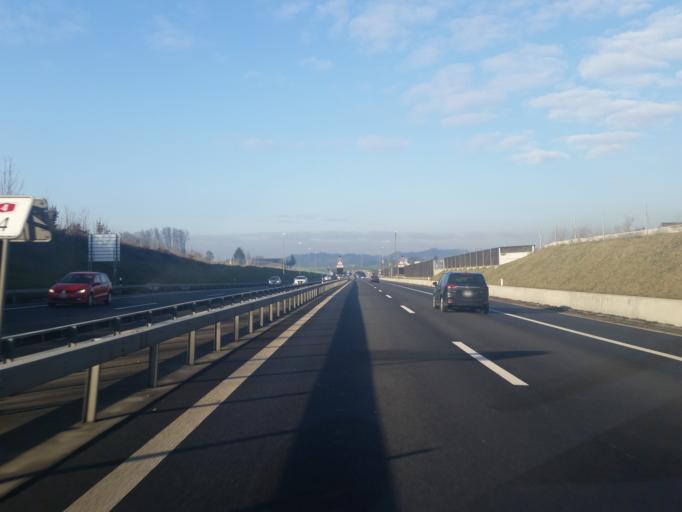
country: CH
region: Zurich
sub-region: Bezirk Affoltern
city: Knonau
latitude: 47.2331
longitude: 8.4582
